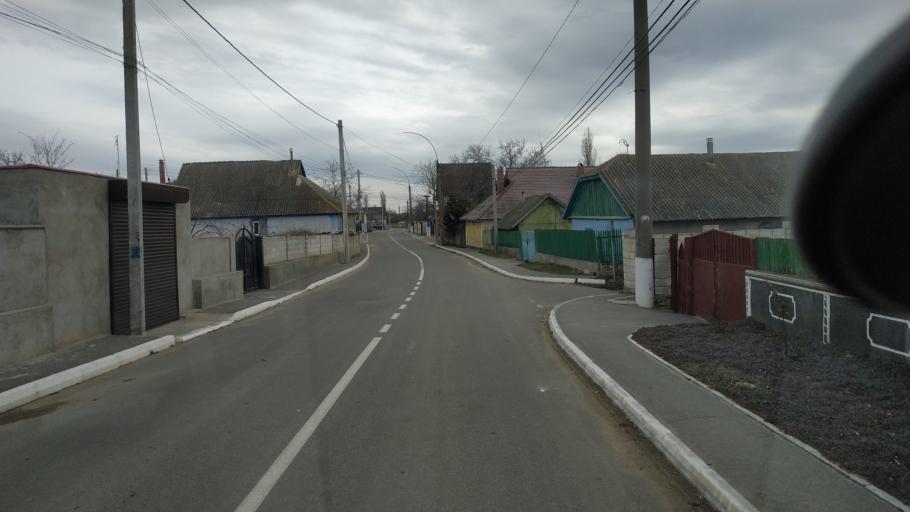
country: MD
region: Telenesti
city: Cocieri
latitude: 47.3485
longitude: 29.1095
